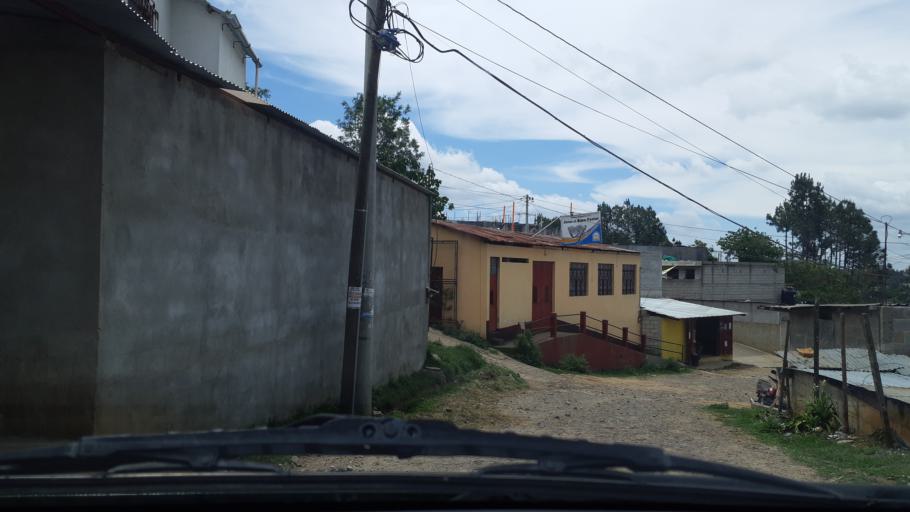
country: GT
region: Chimaltenango
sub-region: Municipio de Chimaltenango
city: Chimaltenango
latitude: 14.6631
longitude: -90.8506
